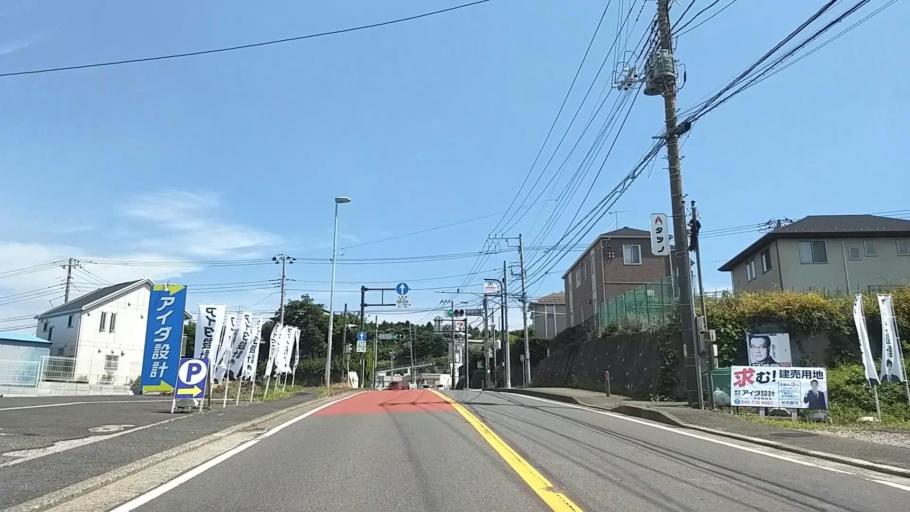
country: JP
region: Kanagawa
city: Fujisawa
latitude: 35.3736
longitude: 139.5093
